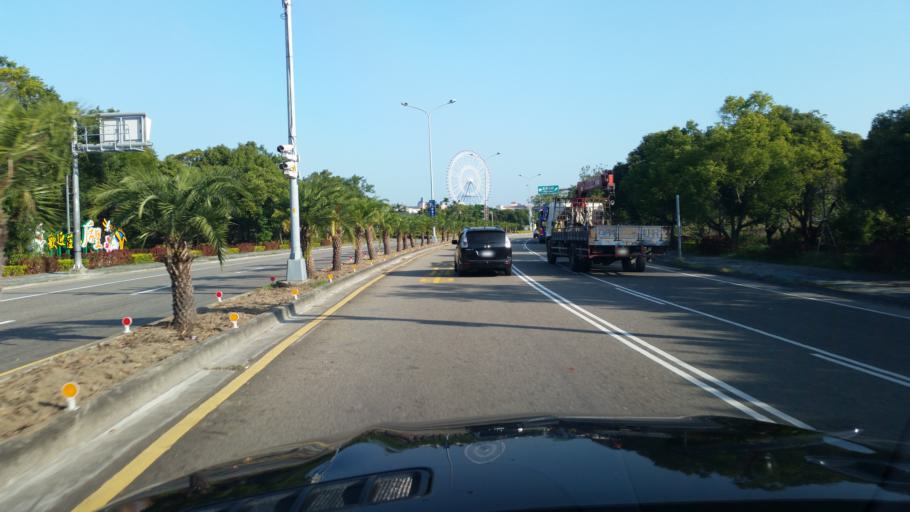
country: TW
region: Taiwan
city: Fengyuan
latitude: 24.3136
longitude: 120.6971
